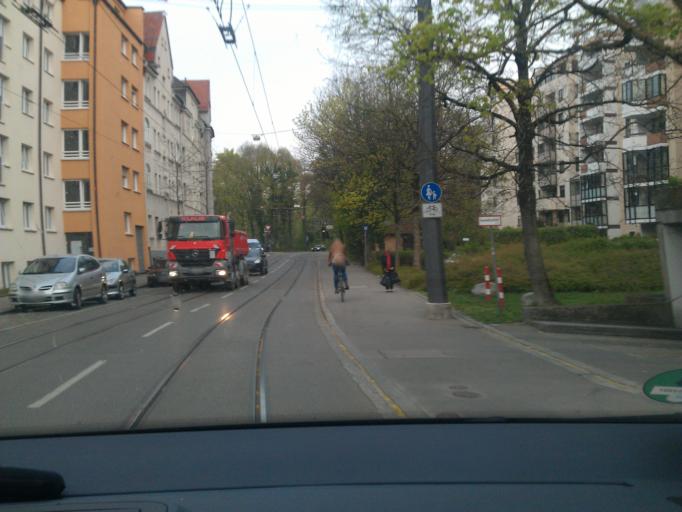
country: DE
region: Bavaria
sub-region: Swabia
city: Augsburg
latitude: 48.3609
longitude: 10.9072
